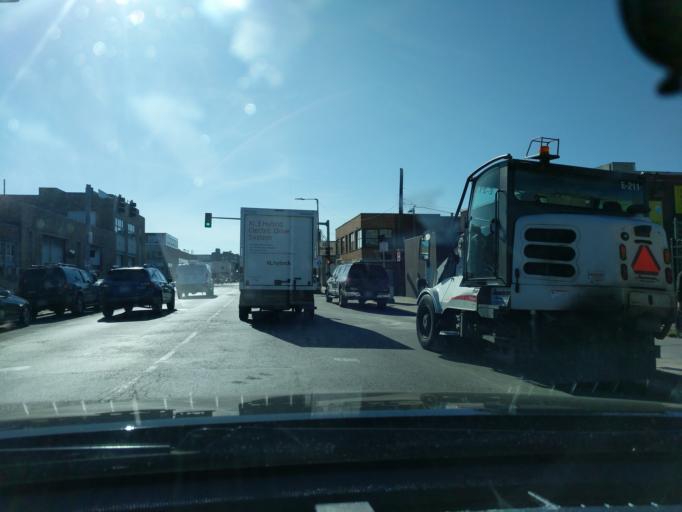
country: US
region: Massachusetts
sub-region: Suffolk County
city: South Boston
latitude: 42.3309
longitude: -71.0703
